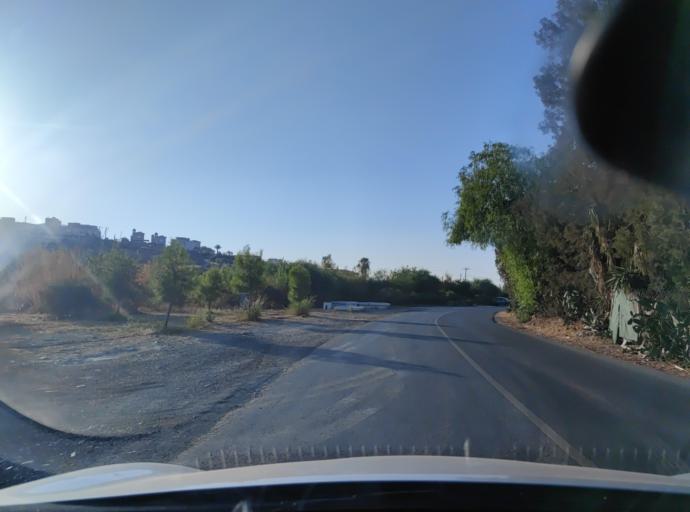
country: CY
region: Limassol
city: Mouttagiaka
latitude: 34.7182
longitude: 33.0889
